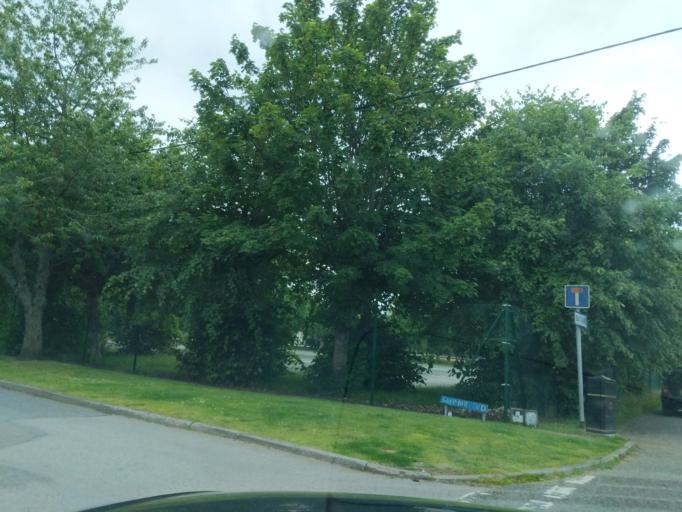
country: GB
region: Scotland
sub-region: Aberdeenshire
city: Ballater
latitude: 57.0462
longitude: -3.0437
